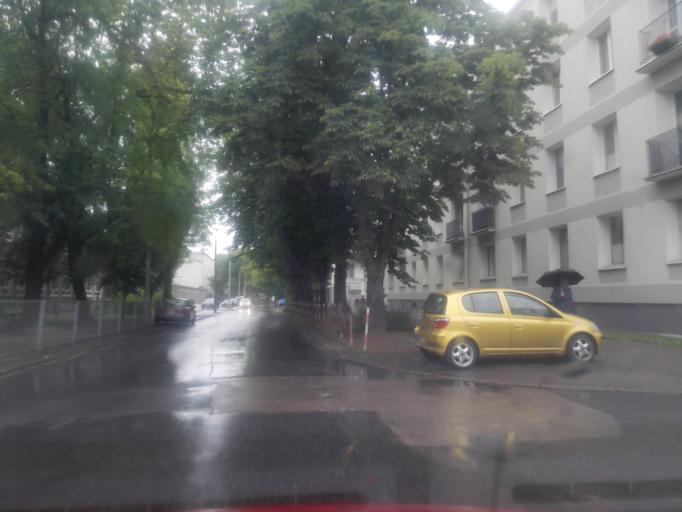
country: PL
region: Masovian Voivodeship
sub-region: Warszawa
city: Mokotow
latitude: 52.1926
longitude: 21.0106
